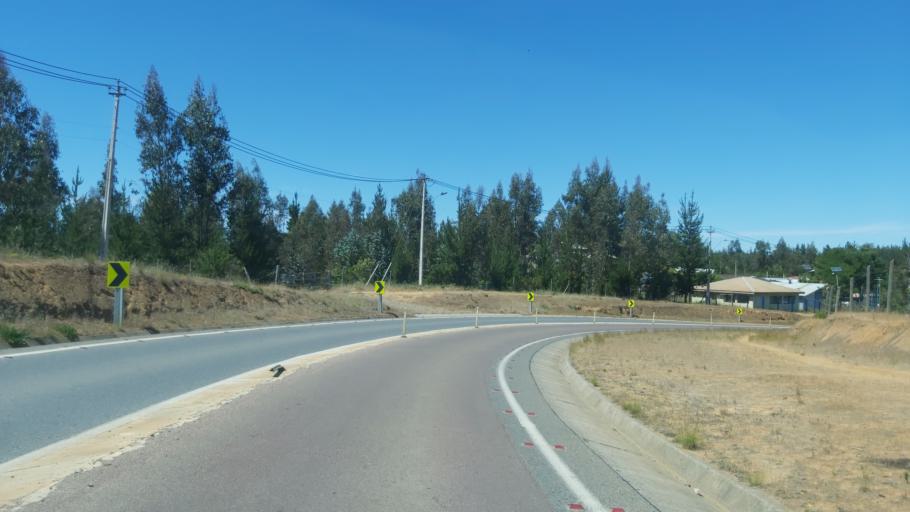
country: CL
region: Maule
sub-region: Provincia de Talca
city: Talca
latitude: -34.9631
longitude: -71.9606
